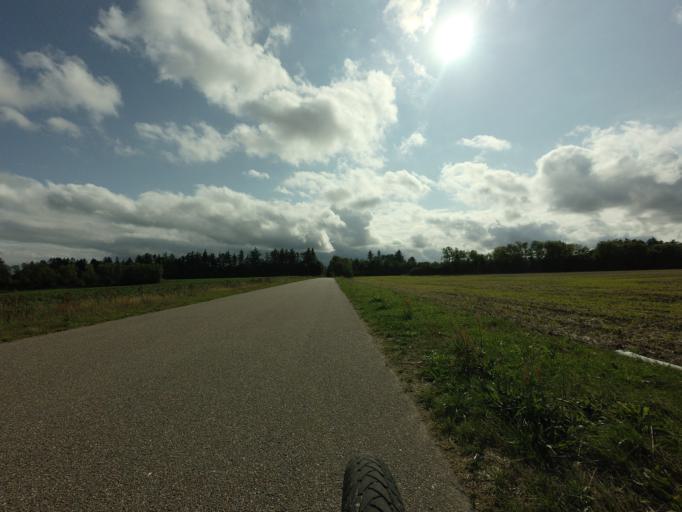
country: DK
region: North Denmark
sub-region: Hjorring Kommune
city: Hirtshals
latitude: 57.5466
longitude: 10.0566
